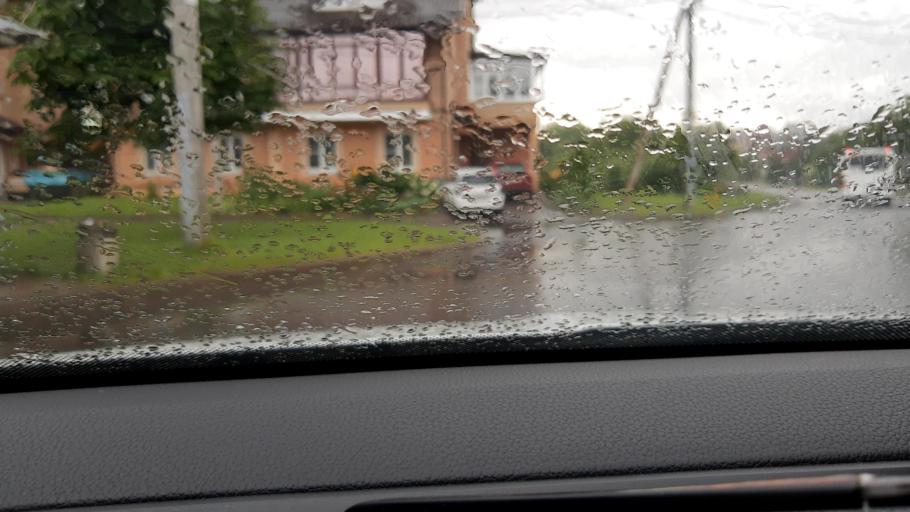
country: RU
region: Moskovskaya
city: Kommunarka
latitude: 55.5343
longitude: 37.4834
